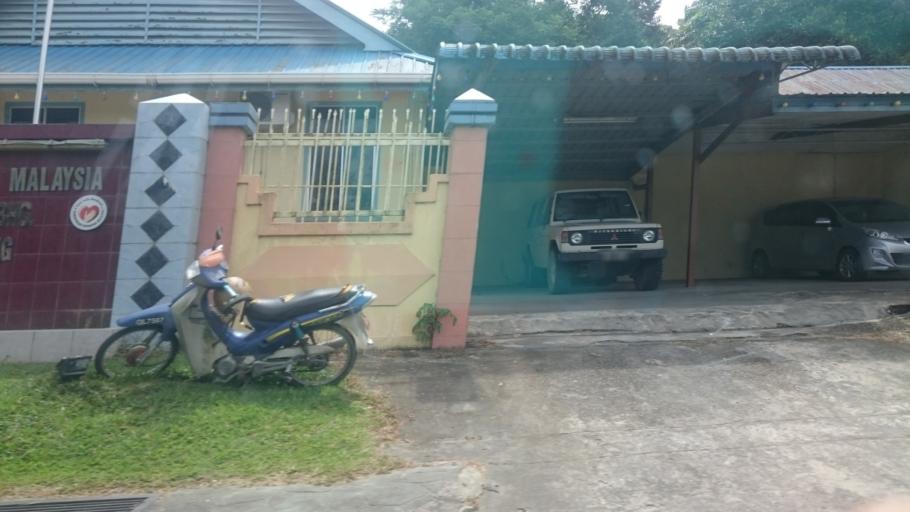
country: MY
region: Sarawak
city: Limbang
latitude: 4.7502
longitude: 115.0074
